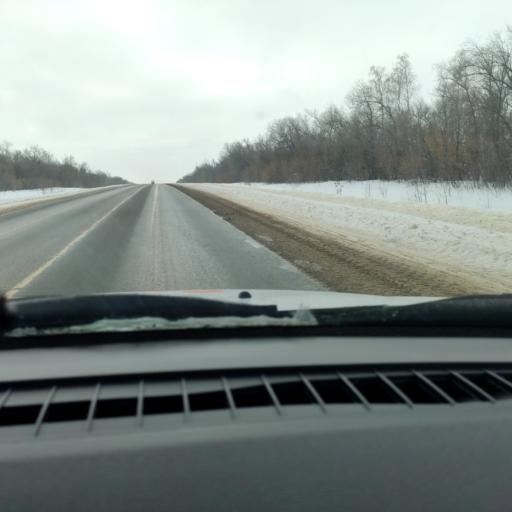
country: RU
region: Samara
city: Dubovyy Umet
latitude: 52.7482
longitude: 50.4927
